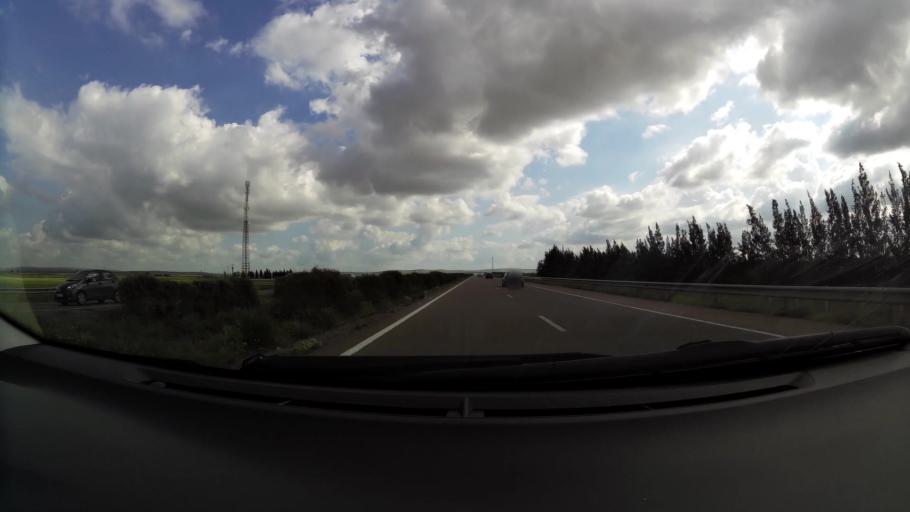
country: MA
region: Chaouia-Ouardigha
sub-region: Settat Province
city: Berrechid
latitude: 33.1445
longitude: -7.5742
